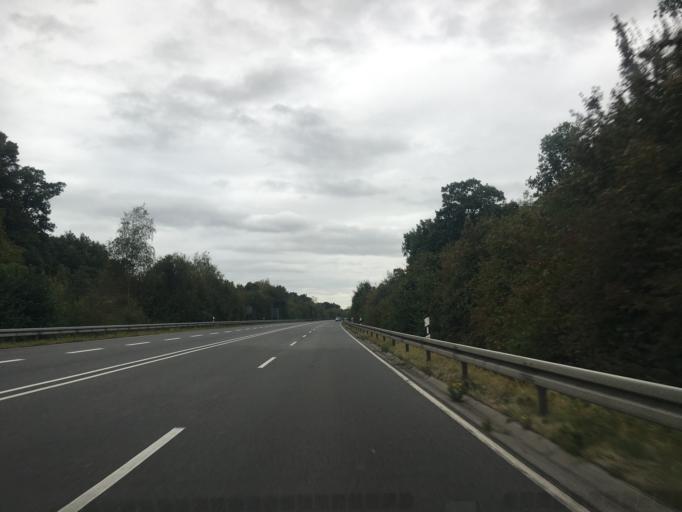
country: DE
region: North Rhine-Westphalia
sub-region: Regierungsbezirk Munster
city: Metelen
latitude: 52.1724
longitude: 7.2580
